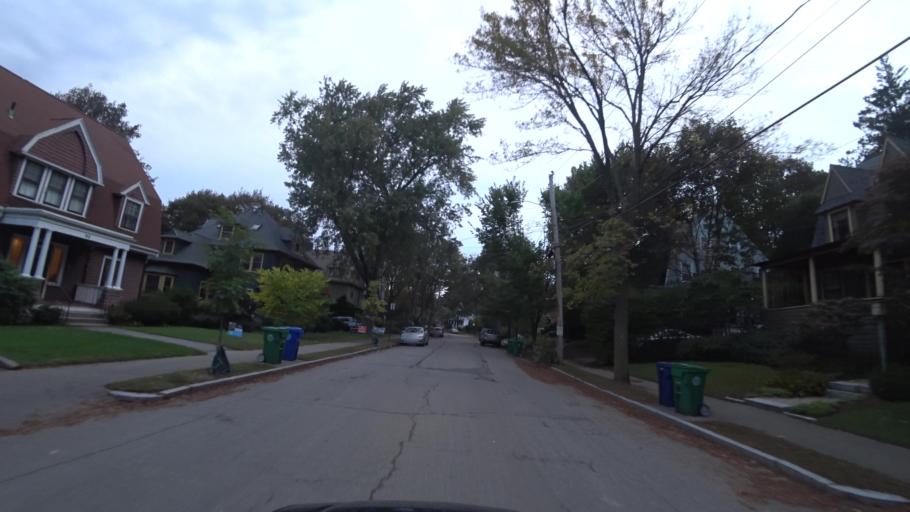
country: US
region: Massachusetts
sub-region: Middlesex County
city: Newton
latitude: 42.3249
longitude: -71.1951
